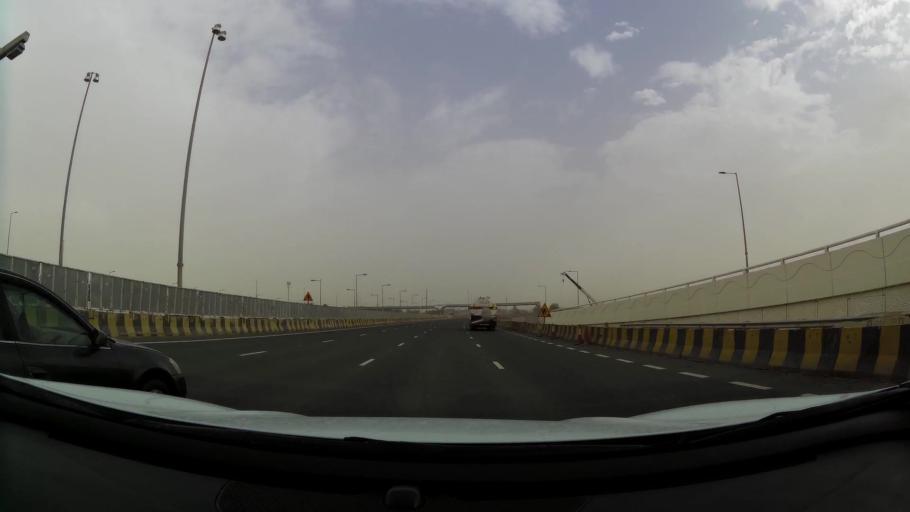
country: AE
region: Abu Dhabi
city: Abu Dhabi
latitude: 24.4675
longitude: 54.6311
